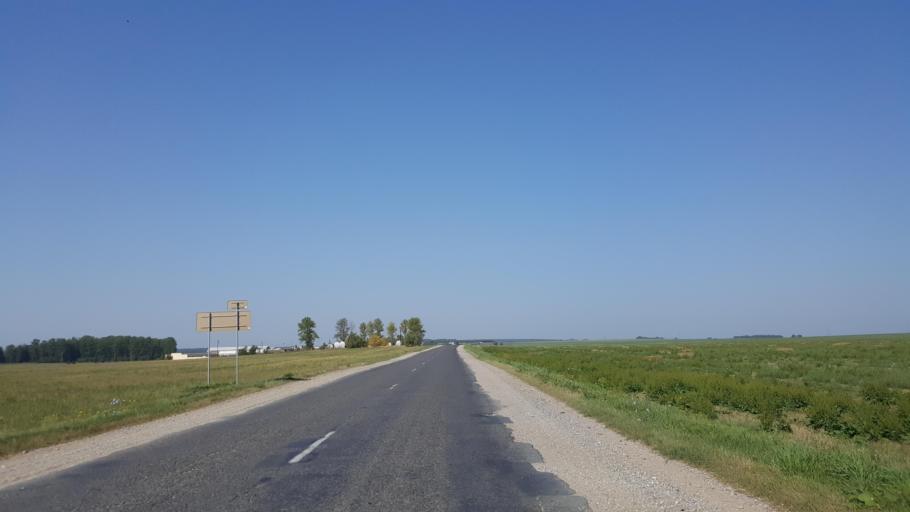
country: BY
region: Brest
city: Kamyanyets
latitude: 52.4153
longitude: 23.6303
